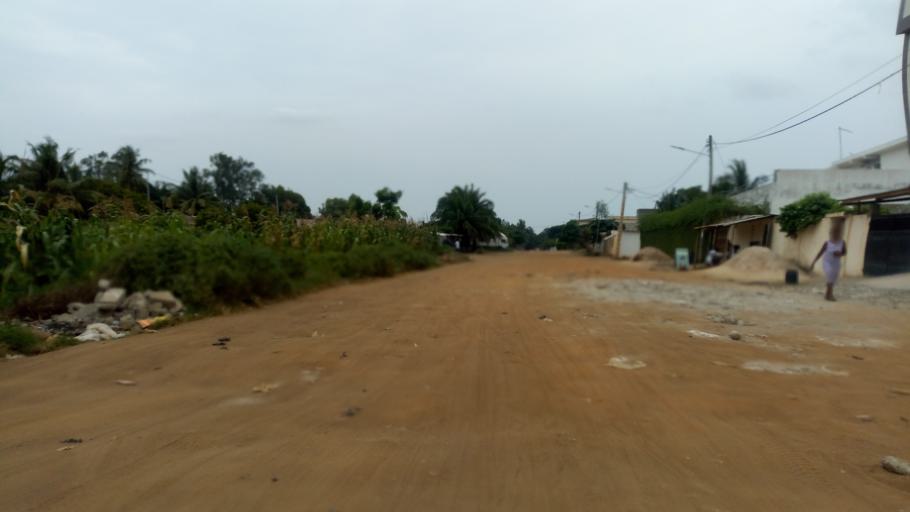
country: TG
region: Maritime
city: Lome
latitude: 6.1810
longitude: 1.1844
